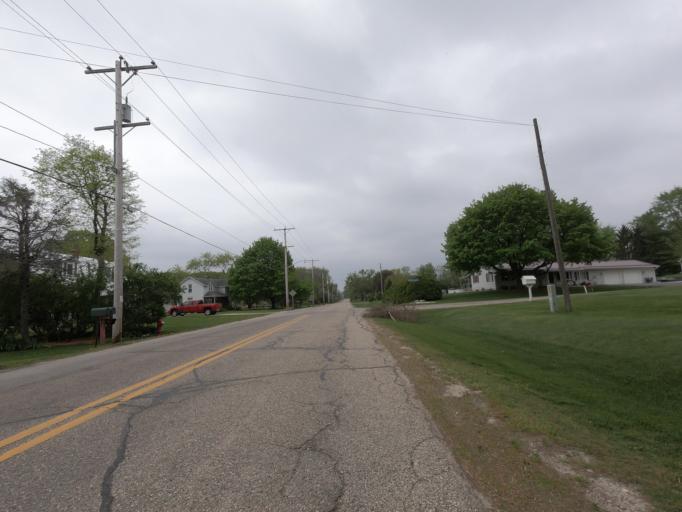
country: US
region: Wisconsin
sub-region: Jefferson County
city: Jefferson
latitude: 43.0282
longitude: -88.8093
